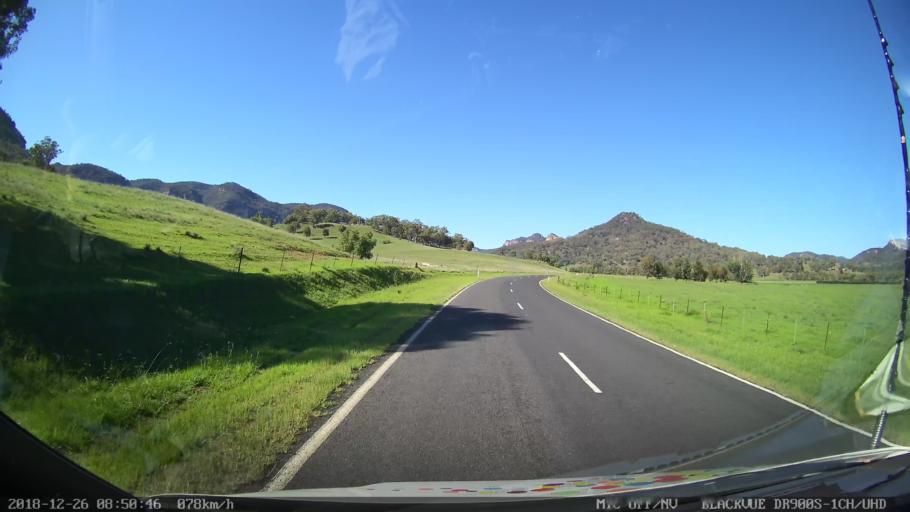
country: AU
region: New South Wales
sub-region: Mid-Western Regional
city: Kandos
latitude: -32.5791
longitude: 150.0930
